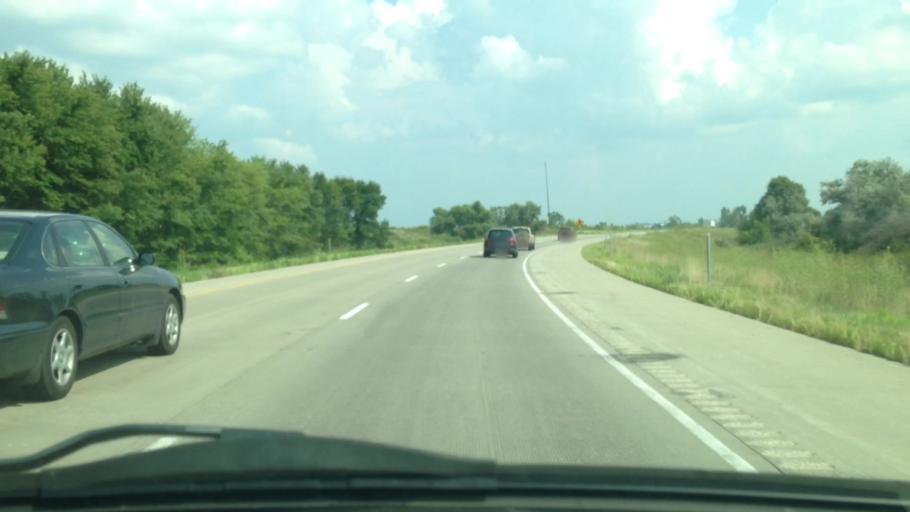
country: US
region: Iowa
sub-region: Black Hawk County
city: Elk Run Heights
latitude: 42.4482
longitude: -92.1952
